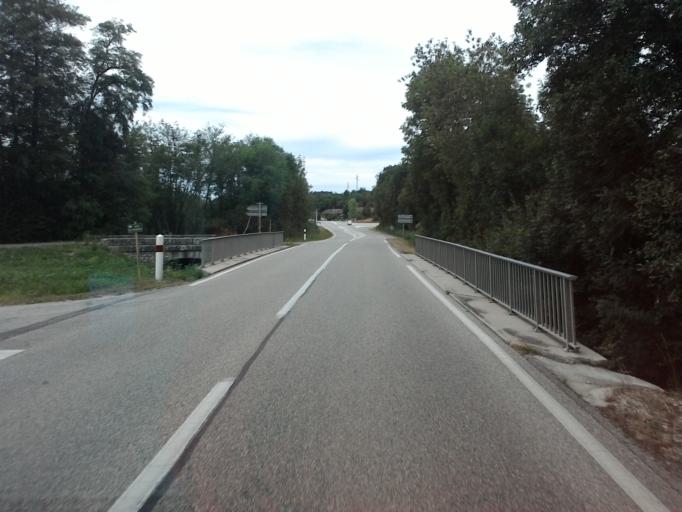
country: FR
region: Rhone-Alpes
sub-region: Departement de l'Isere
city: Morestel
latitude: 45.7070
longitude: 5.4448
